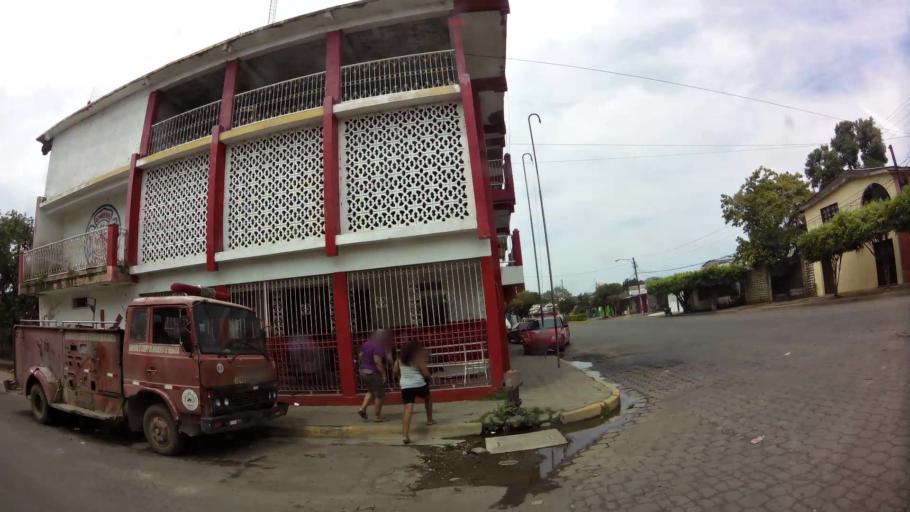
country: NI
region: Rivas
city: Rivas
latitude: 11.4412
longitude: -85.8267
